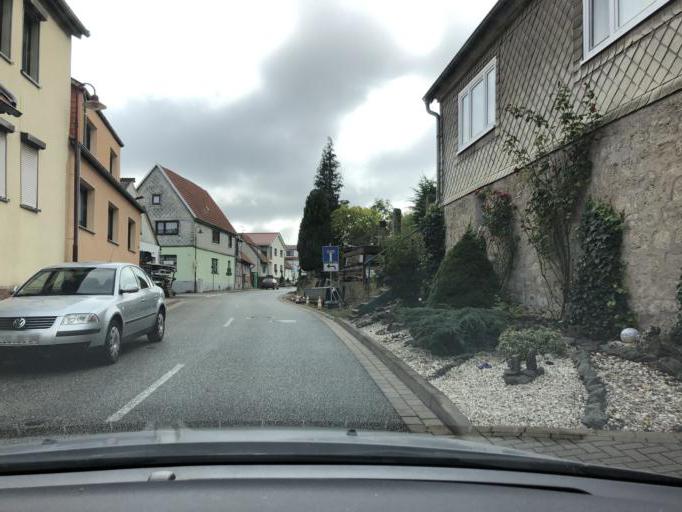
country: DE
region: Thuringia
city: Heuthen
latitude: 51.3312
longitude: 10.2224
